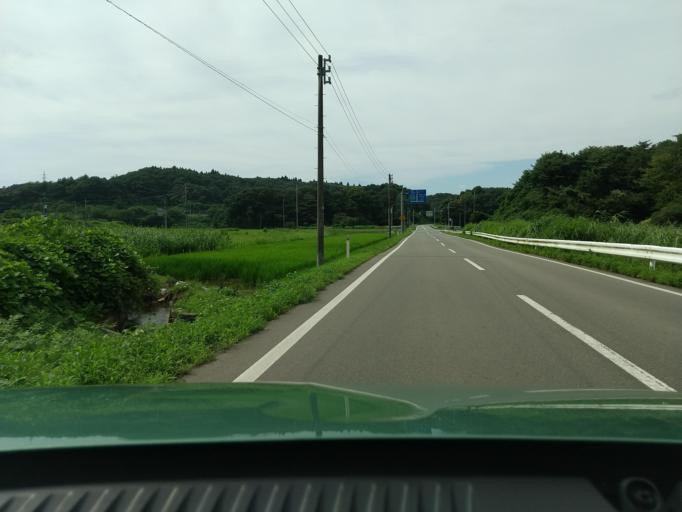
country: JP
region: Akita
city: Akita
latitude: 39.7219
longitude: 140.1858
